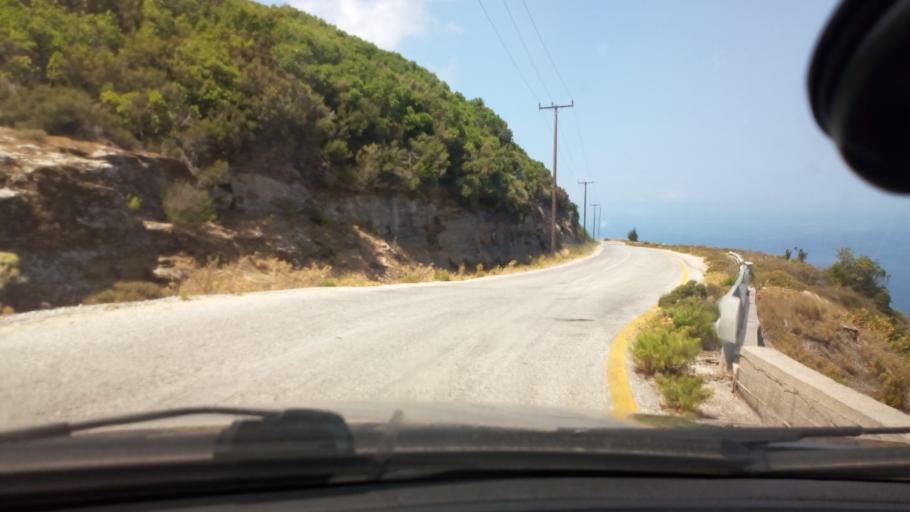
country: GR
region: North Aegean
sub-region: Nomos Samou
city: Agios Kirykos
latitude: 37.6505
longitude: 26.2836
